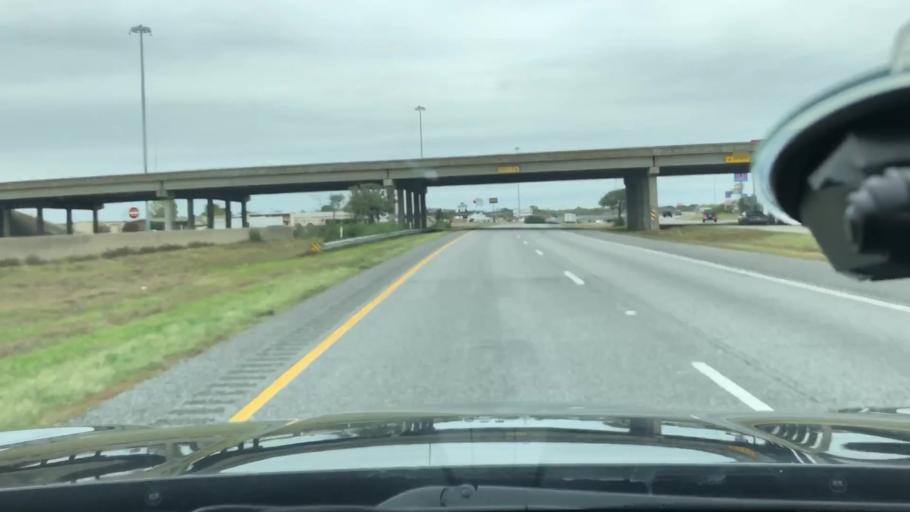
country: US
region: Texas
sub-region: Hunt County
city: Greenville
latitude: 33.1154
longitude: -96.1001
